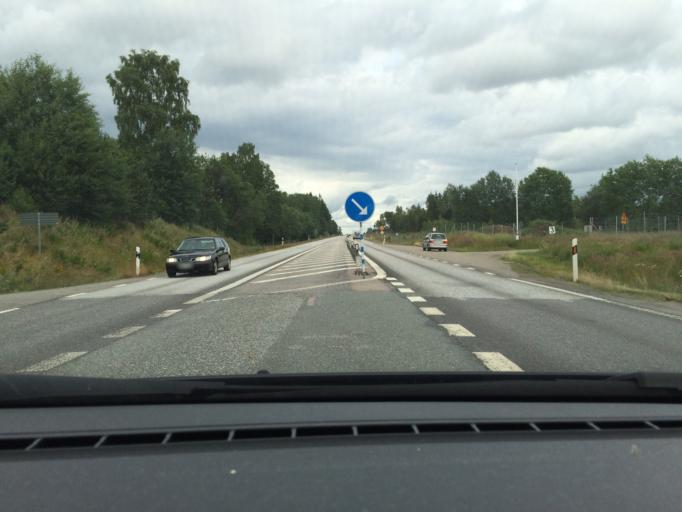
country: SE
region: Joenkoeping
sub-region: Varnamo Kommun
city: Varnamo
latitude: 57.1800
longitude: 13.9324
